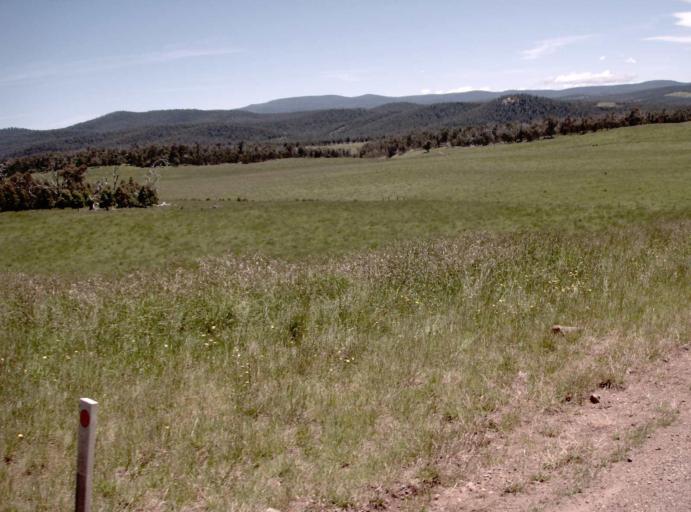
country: AU
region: New South Wales
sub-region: Snowy River
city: Jindabyne
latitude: -37.0915
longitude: 148.2543
